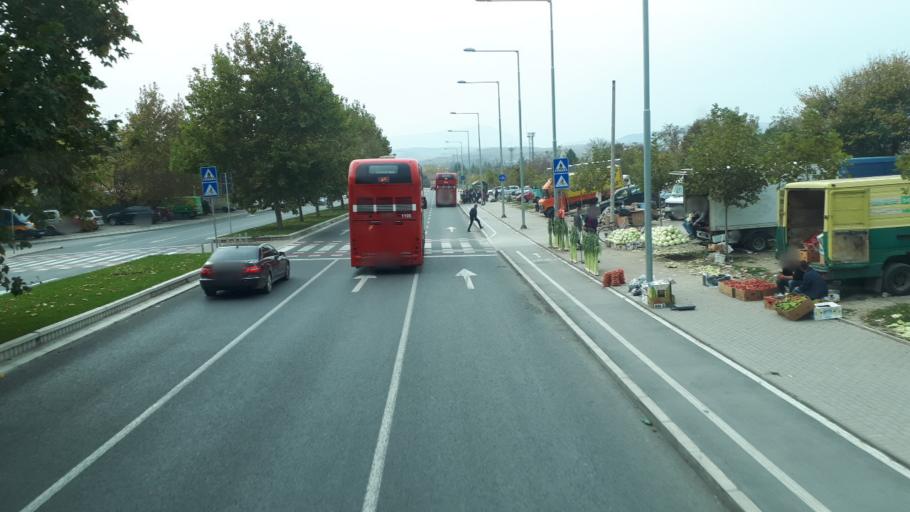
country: MK
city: Krushopek
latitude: 42.0094
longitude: 21.3661
